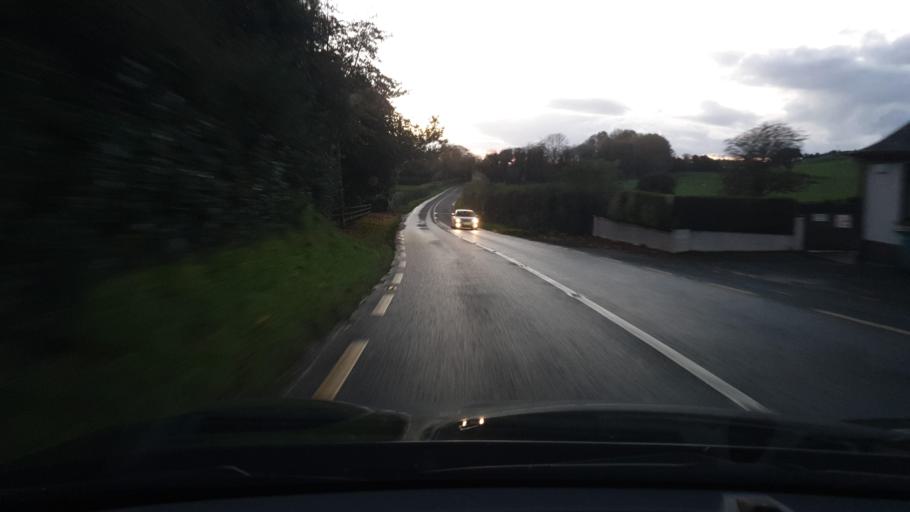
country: IE
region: Leinster
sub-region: An Mhi
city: Slane
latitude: 53.7079
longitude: -6.5226
